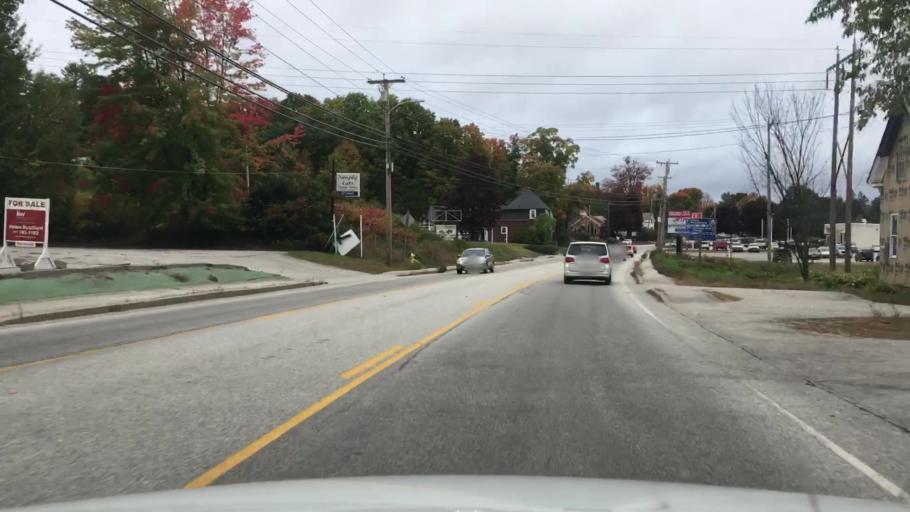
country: US
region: Maine
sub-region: Oxford County
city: Norway
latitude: 44.2018
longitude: -70.5308
